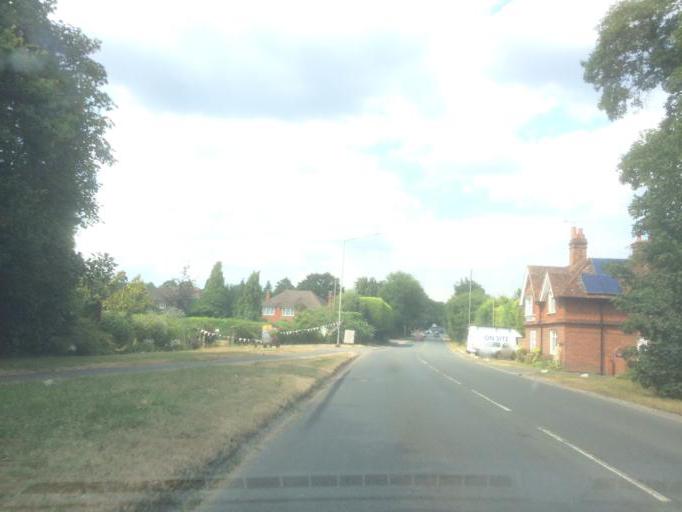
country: GB
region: England
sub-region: Buckinghamshire
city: Farnham Royal
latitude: 51.5449
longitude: -0.6159
